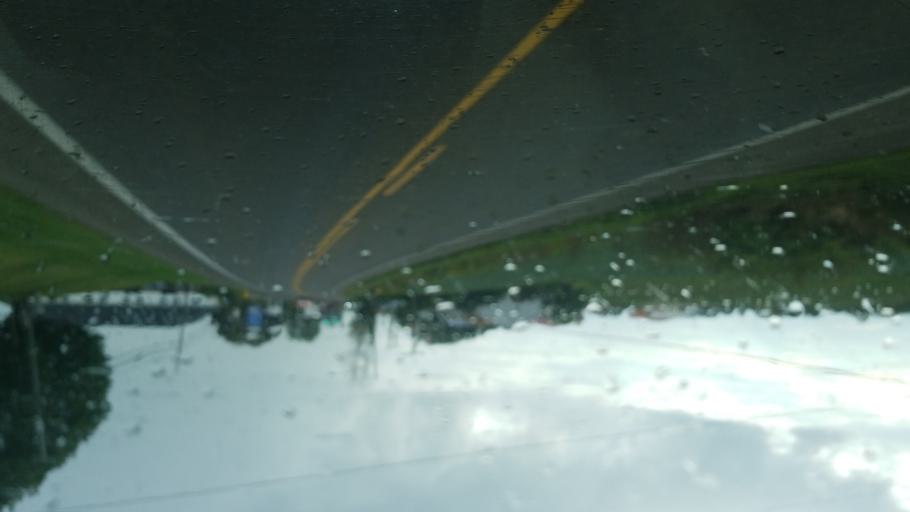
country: US
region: Ohio
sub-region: Holmes County
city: Millersburg
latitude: 40.5586
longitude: -81.7901
